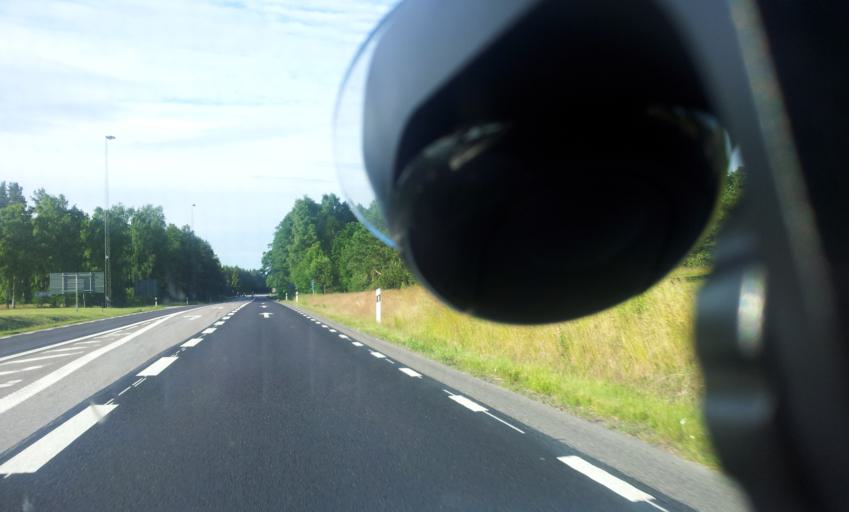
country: SE
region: Kalmar
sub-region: Monsteras Kommun
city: Moensteras
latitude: 57.0249
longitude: 16.4304
